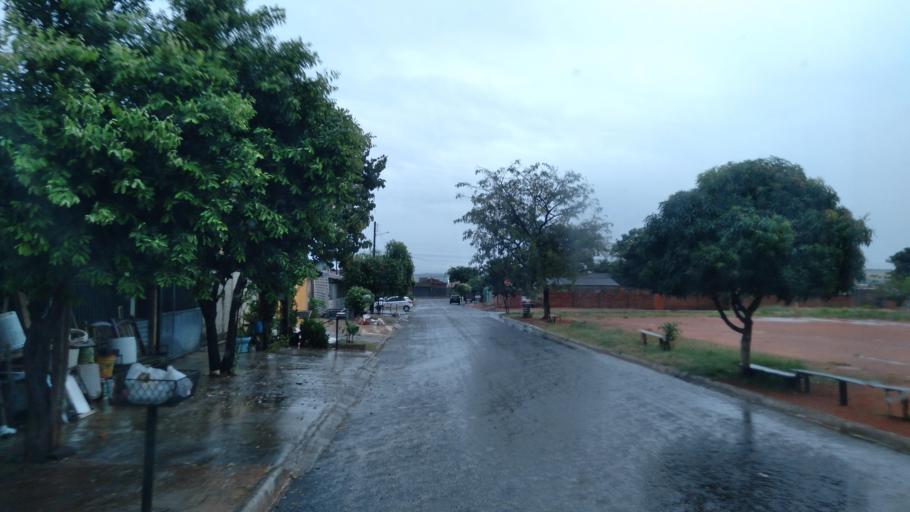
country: BR
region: Goias
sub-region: Mineiros
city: Mineiros
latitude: -17.5412
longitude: -52.5444
